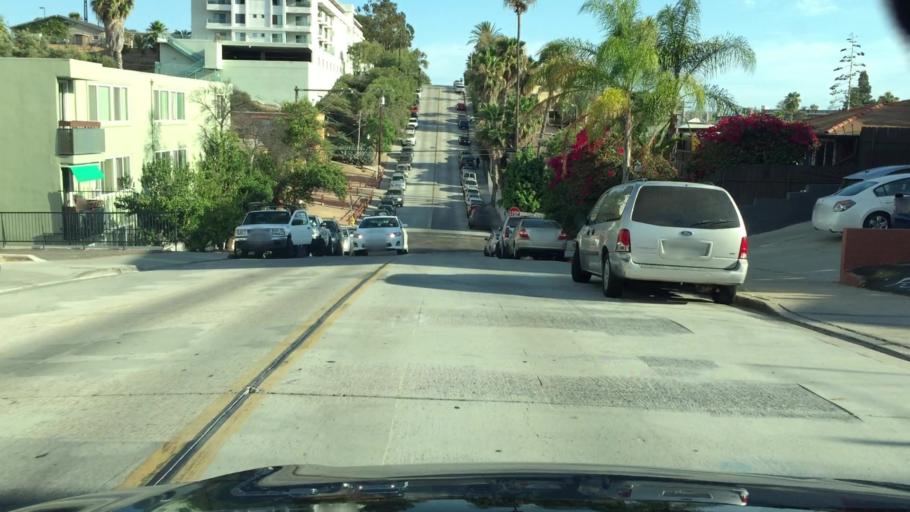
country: US
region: California
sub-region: San Diego County
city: Lemon Grove
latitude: 32.7555
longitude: -117.0837
